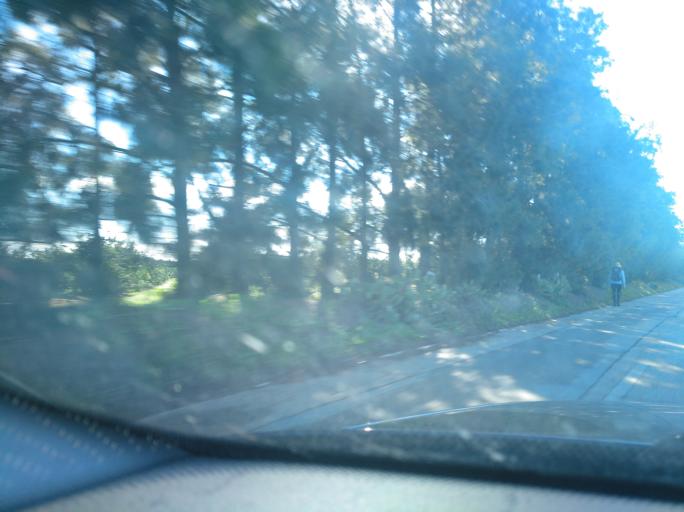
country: PT
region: Faro
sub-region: Vila Real de Santo Antonio
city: Monte Gordo
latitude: 37.1679
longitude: -7.5398
